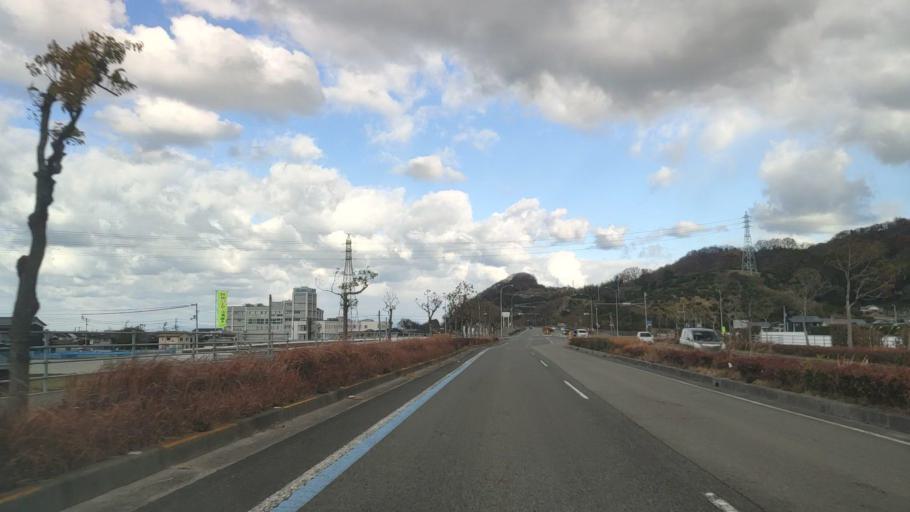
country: JP
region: Ehime
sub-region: Shikoku-chuo Shi
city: Matsuyama
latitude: 33.9014
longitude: 132.7569
